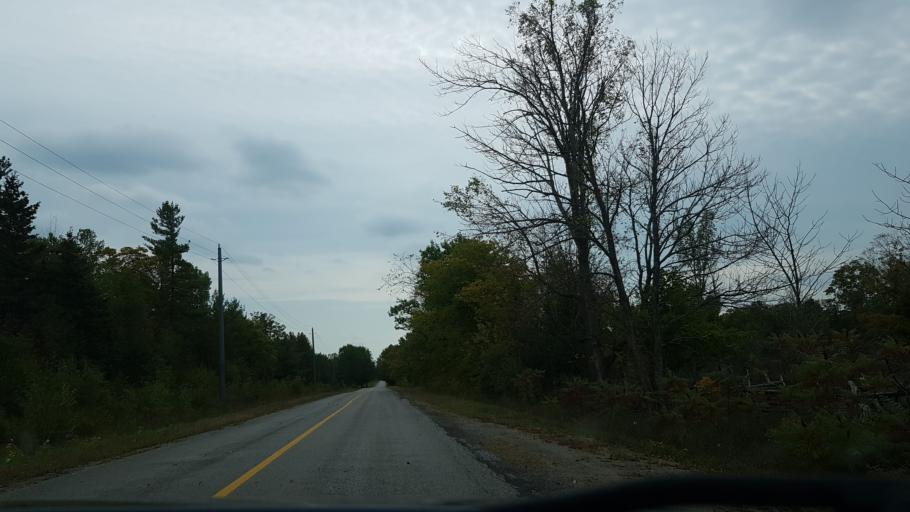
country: CA
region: Ontario
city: Orillia
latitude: 44.6649
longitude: -78.9717
